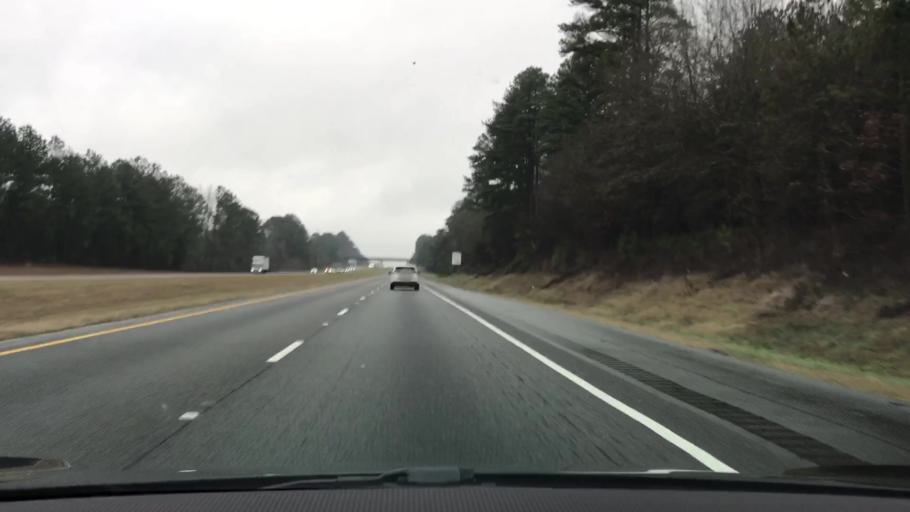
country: US
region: Georgia
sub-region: Walton County
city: Social Circle
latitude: 33.6113
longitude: -83.7124
